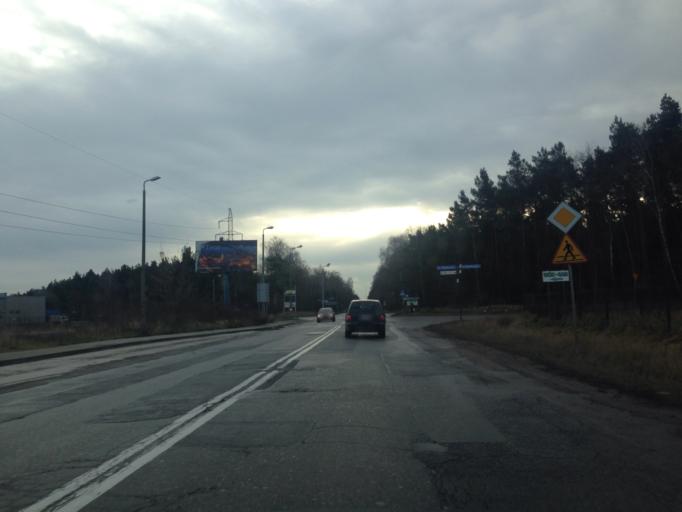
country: PL
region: Kujawsko-Pomorskie
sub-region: Torun
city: Torun
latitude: 52.9900
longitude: 18.6632
